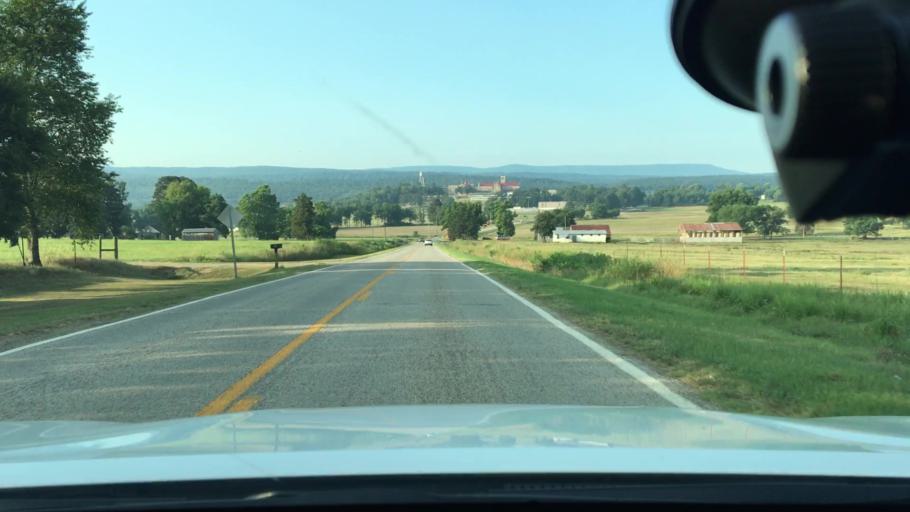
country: US
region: Arkansas
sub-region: Logan County
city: Paris
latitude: 35.3119
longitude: -93.6327
